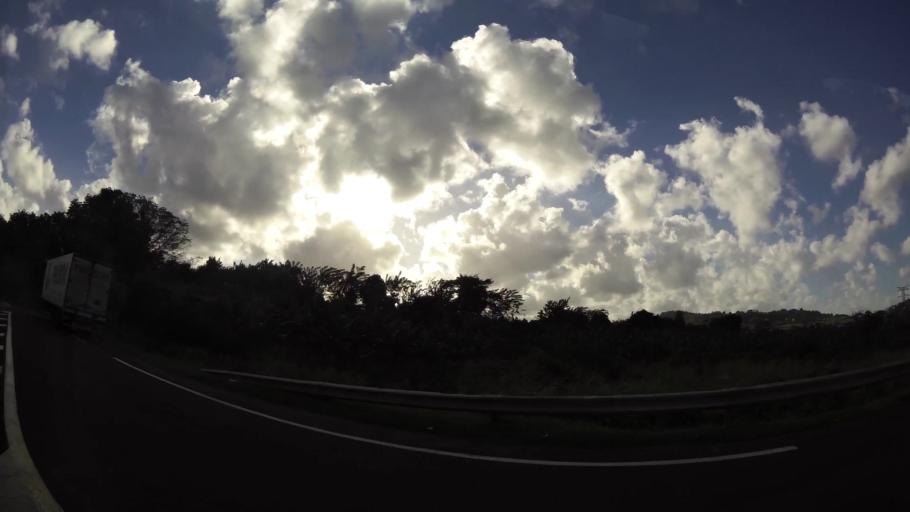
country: MQ
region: Martinique
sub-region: Martinique
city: Ducos
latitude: 14.6021
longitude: -60.9646
